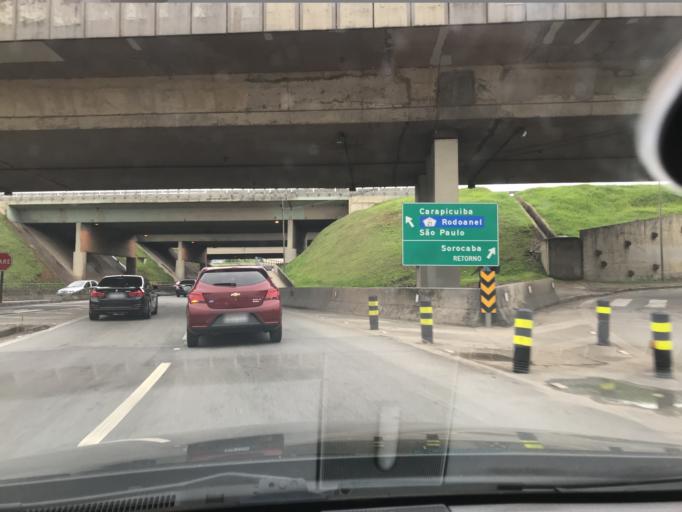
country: BR
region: Sao Paulo
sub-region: Carapicuiba
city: Carapicuiba
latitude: -23.5067
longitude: -46.8330
